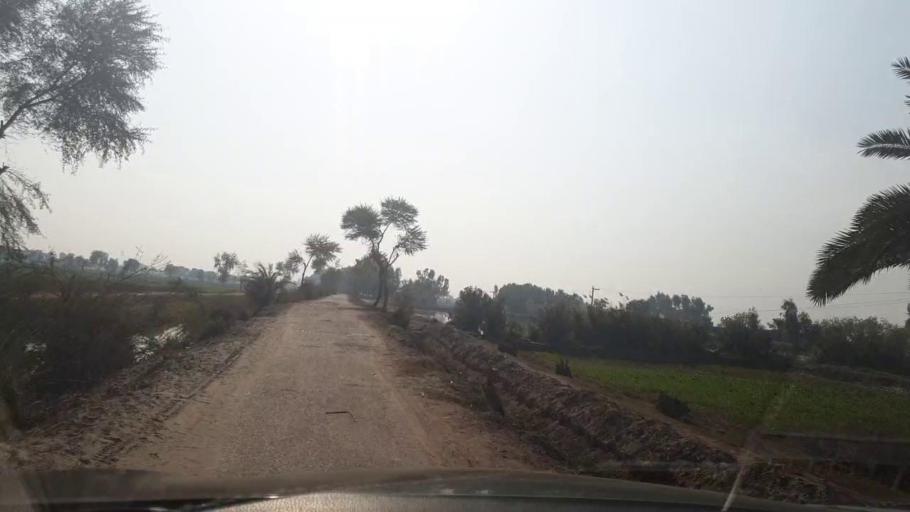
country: PK
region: Sindh
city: Khairpur
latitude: 28.1129
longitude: 69.6392
